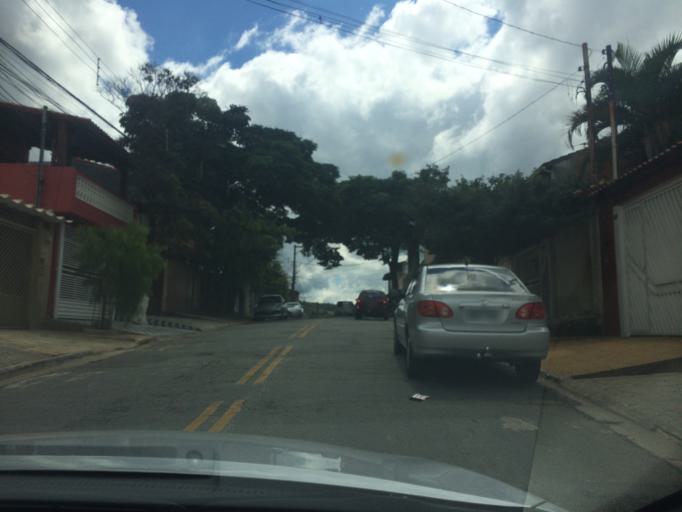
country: BR
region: Sao Paulo
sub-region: Guarulhos
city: Guarulhos
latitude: -23.4298
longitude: -46.5267
